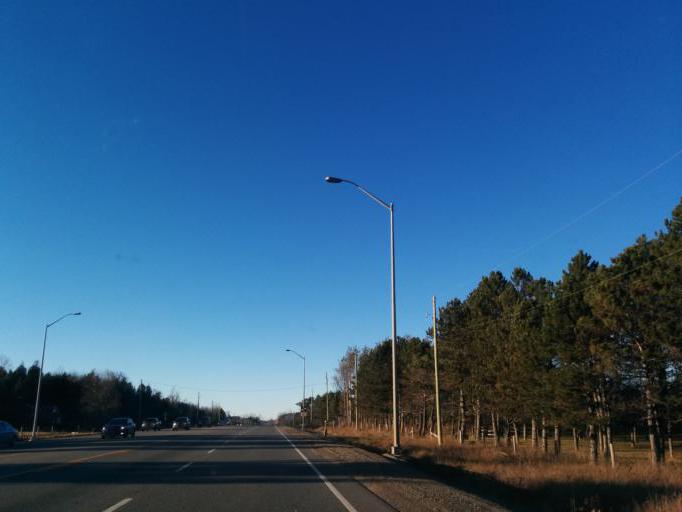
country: CA
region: Ontario
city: Orangeville
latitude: 43.9027
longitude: -80.0536
